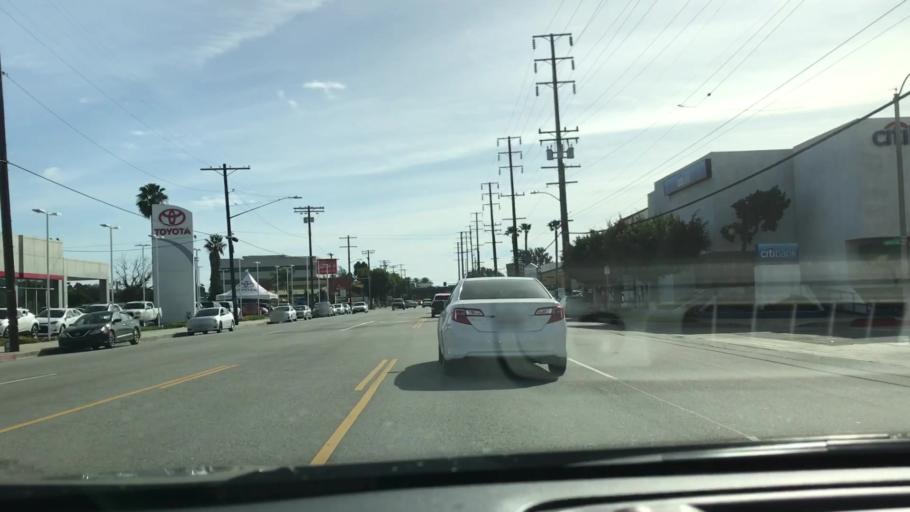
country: US
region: California
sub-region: Los Angeles County
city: Gardena
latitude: 33.8634
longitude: -118.3092
